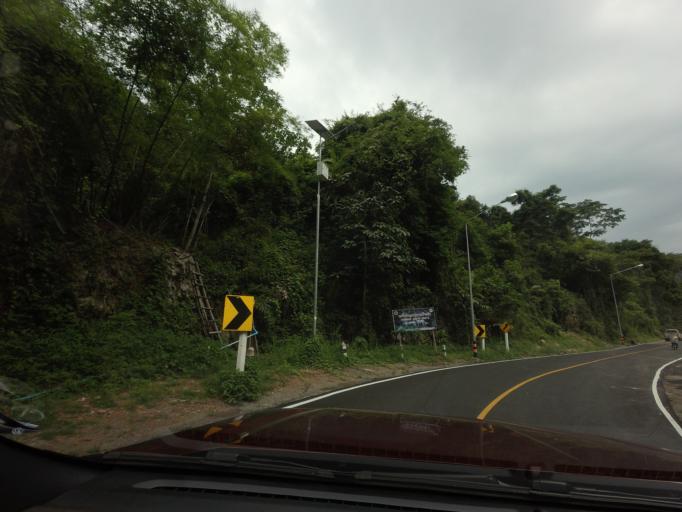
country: TH
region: Yala
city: Than To
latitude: 6.1362
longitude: 101.3021
